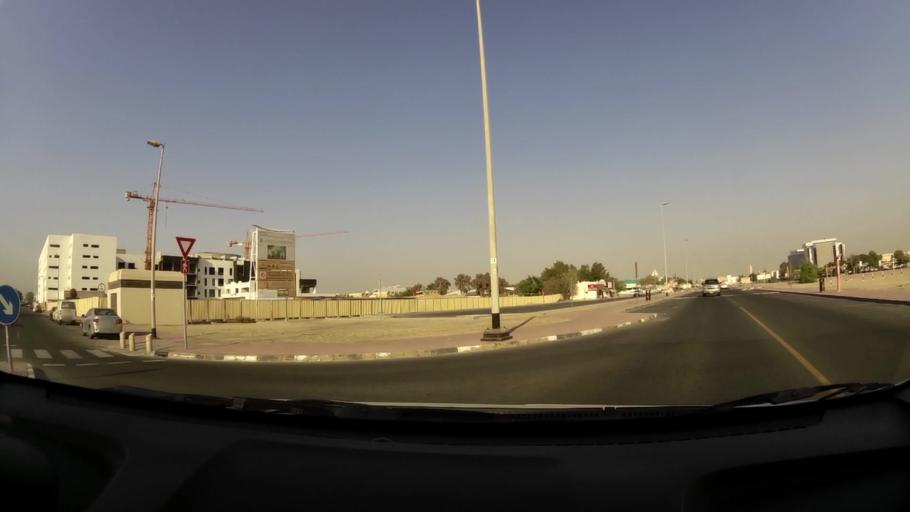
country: AE
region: Ash Shariqah
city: Sharjah
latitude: 25.2660
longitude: 55.3874
